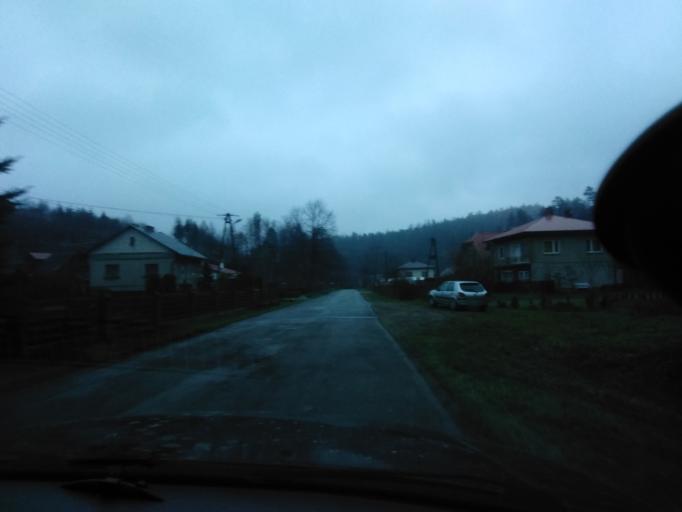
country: PL
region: Subcarpathian Voivodeship
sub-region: Powiat brzozowski
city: Nozdrzec
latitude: 49.7557
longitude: 22.1465
